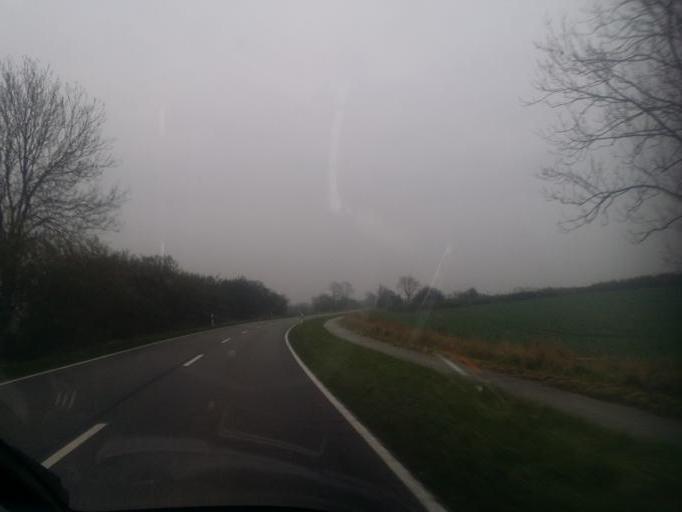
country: DE
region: Schleswig-Holstein
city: Grosssolt
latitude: 54.6929
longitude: 9.4985
